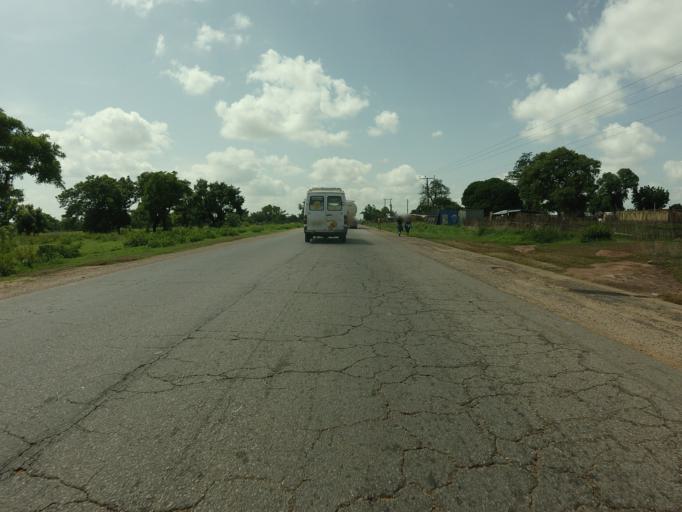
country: GH
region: Northern
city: Savelugu
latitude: 9.5769
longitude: -0.8342
